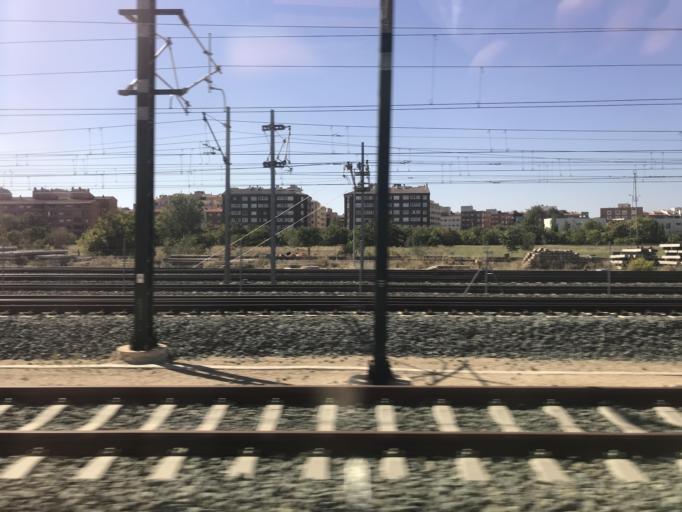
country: ES
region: Castille-La Mancha
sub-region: Provincia de Albacete
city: Albacete
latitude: 39.0030
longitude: -1.8501
